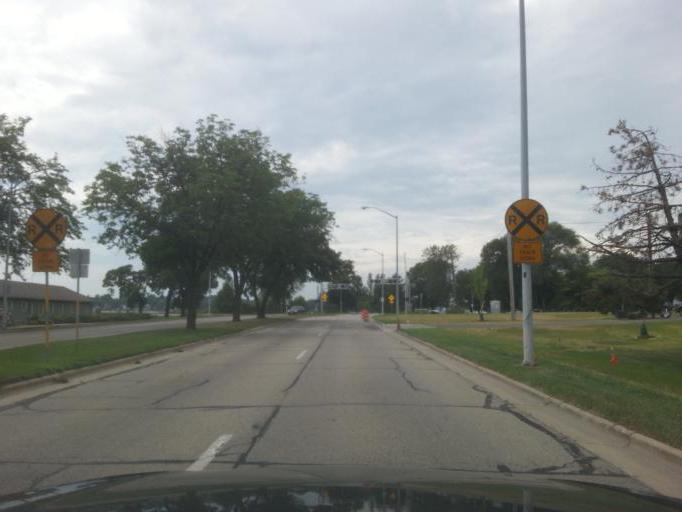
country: US
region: Wisconsin
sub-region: Dane County
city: Madison
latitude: 43.0654
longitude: -89.3892
